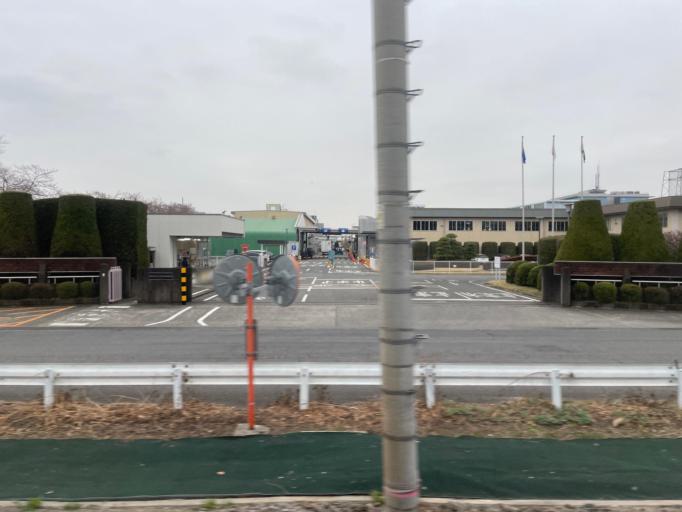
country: JP
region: Gunma
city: Maebashi-shi
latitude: 36.3998
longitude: 139.0437
